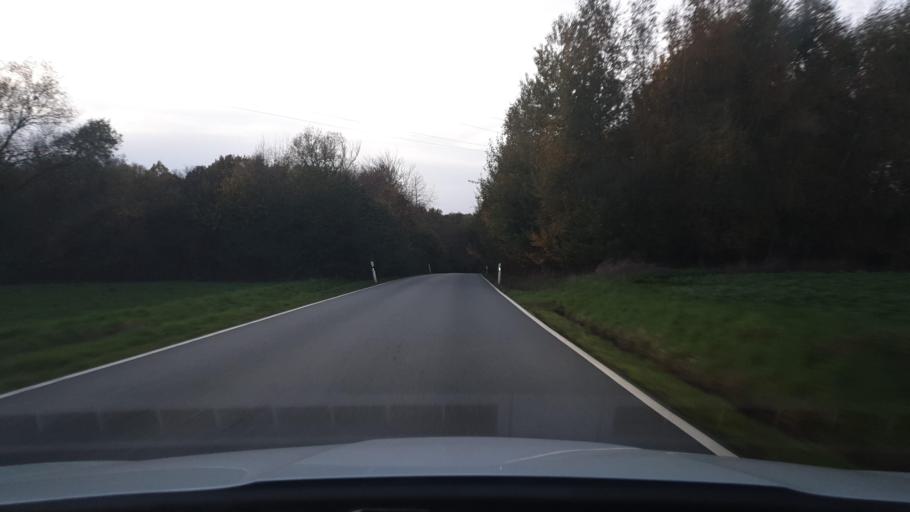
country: DE
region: North Rhine-Westphalia
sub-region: Regierungsbezirk Detmold
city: Bielefeld
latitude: 52.0617
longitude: 8.5706
